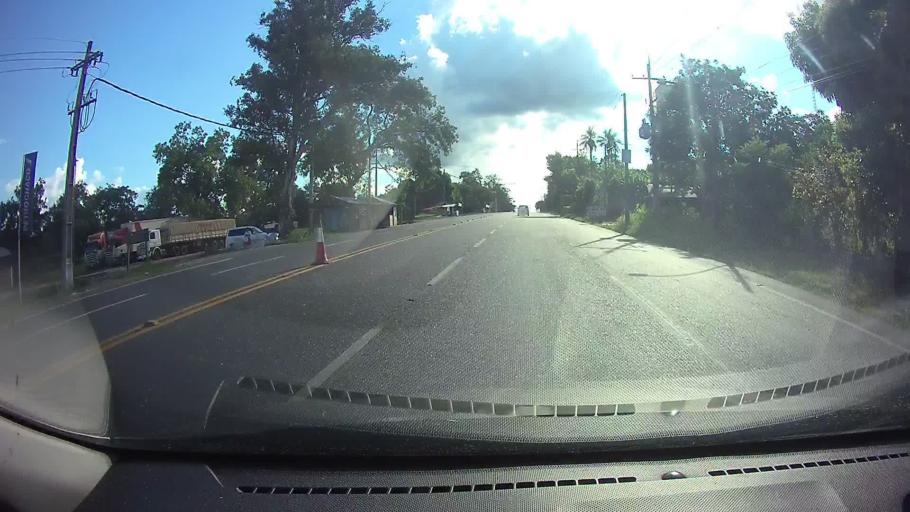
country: PY
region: Cordillera
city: Eusebio Ayala
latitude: -25.3823
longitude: -57.0455
